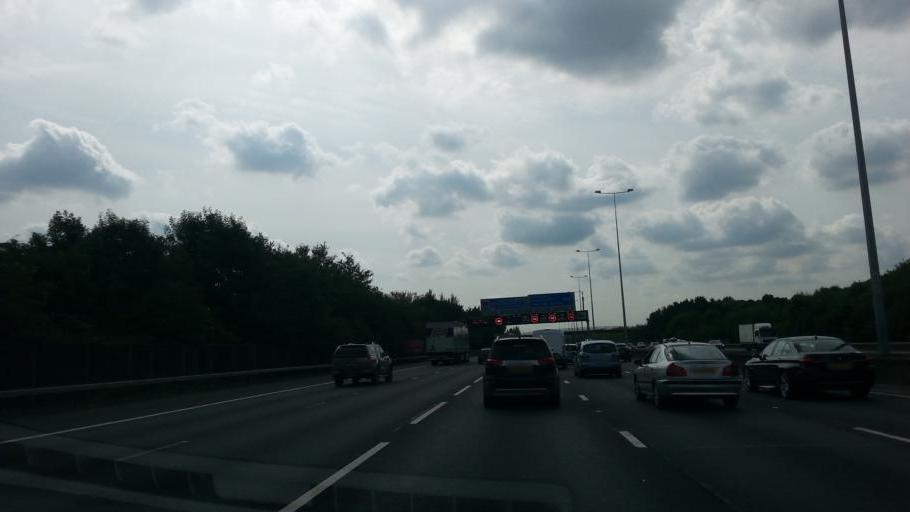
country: GB
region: England
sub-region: Surrey
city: Egham
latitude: 51.4169
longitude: -0.5396
